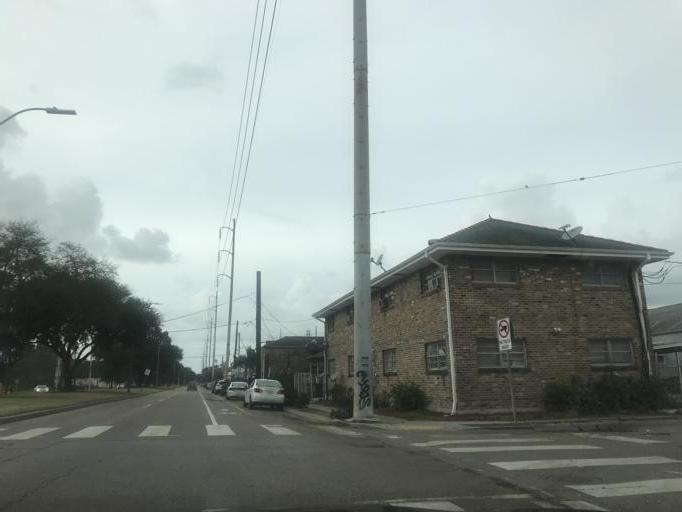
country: US
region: Louisiana
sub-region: Orleans Parish
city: New Orleans
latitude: 29.9475
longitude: -90.0902
